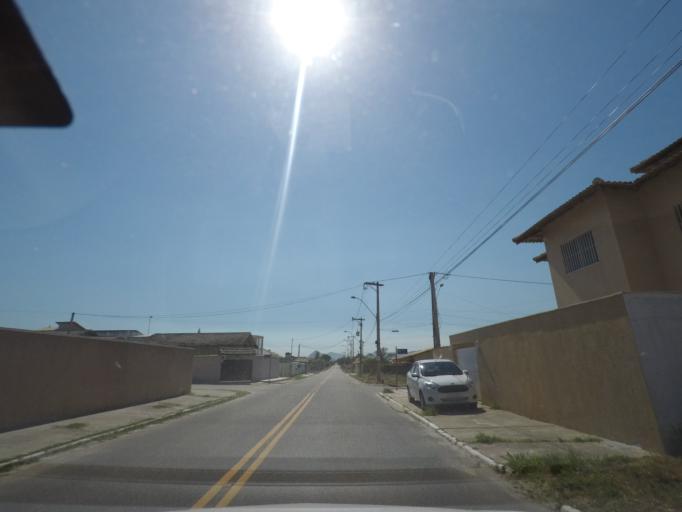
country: BR
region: Rio de Janeiro
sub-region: Marica
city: Marica
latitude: -22.9669
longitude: -42.9089
